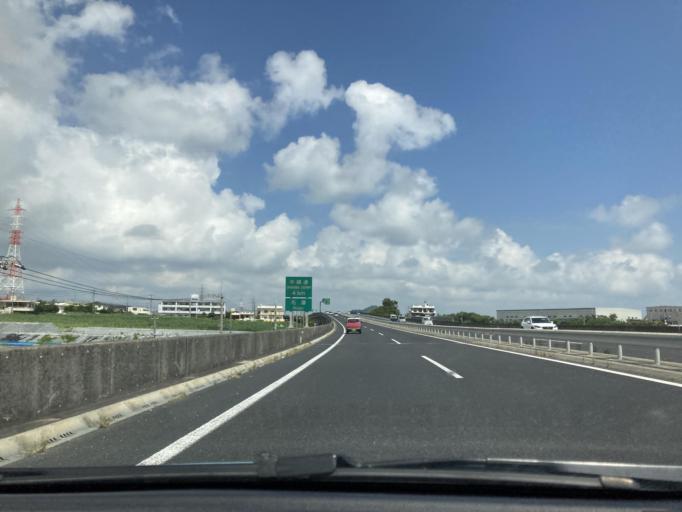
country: JP
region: Okinawa
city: Tomigusuku
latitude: 26.1872
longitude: 127.7374
